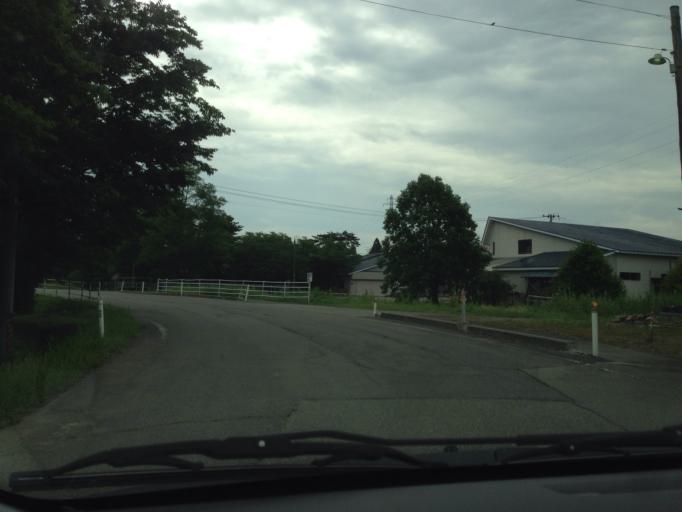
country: JP
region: Fukushima
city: Inawashiro
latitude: 37.5518
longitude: 140.0551
